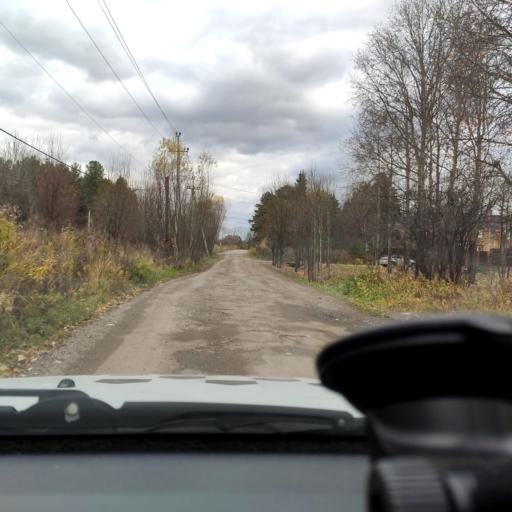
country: RU
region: Perm
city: Perm
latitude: 57.9944
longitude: 56.3321
